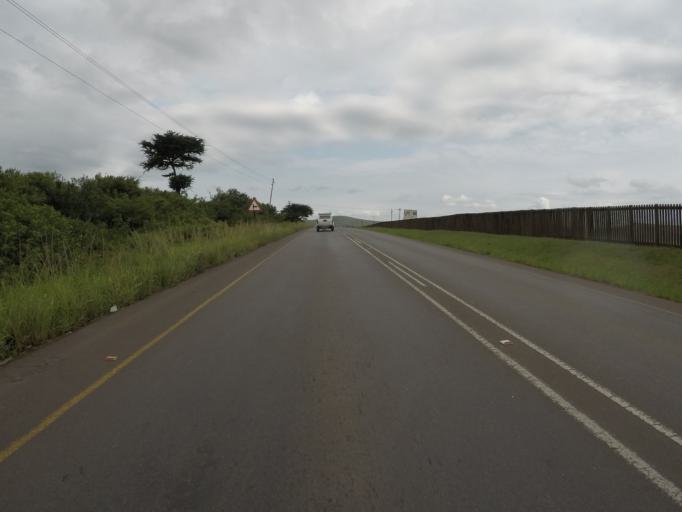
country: ZA
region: KwaZulu-Natal
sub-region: uThungulu District Municipality
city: Empangeni
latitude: -28.7272
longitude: 31.8687
